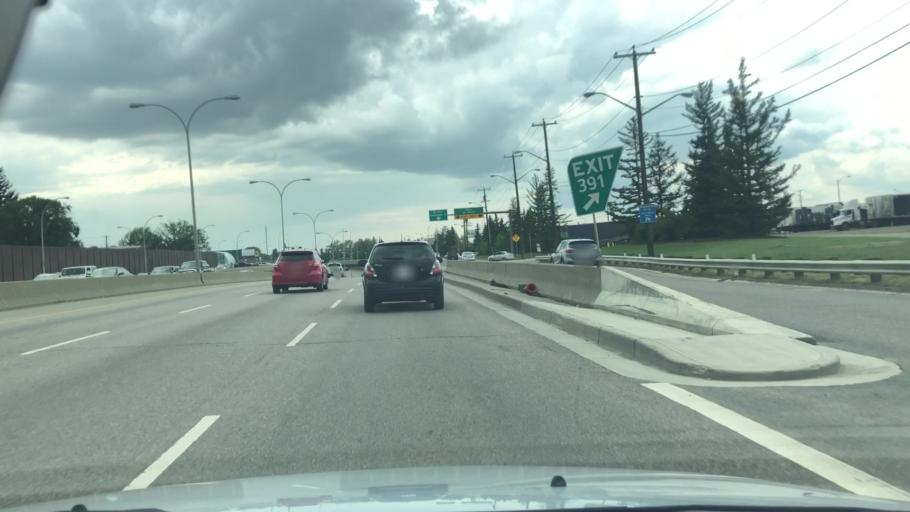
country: CA
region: Alberta
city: Edmonton
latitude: 53.5824
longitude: -113.4633
